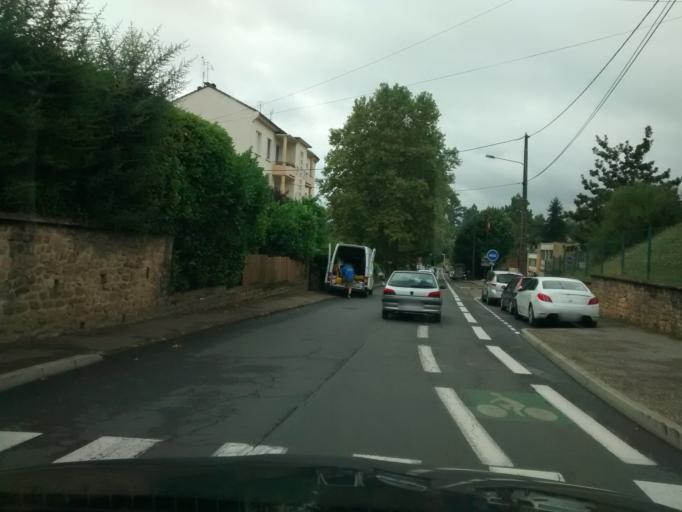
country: FR
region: Aquitaine
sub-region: Departement de la Dordogne
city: Sarlat-la-Caneda
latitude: 44.8833
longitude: 1.2160
